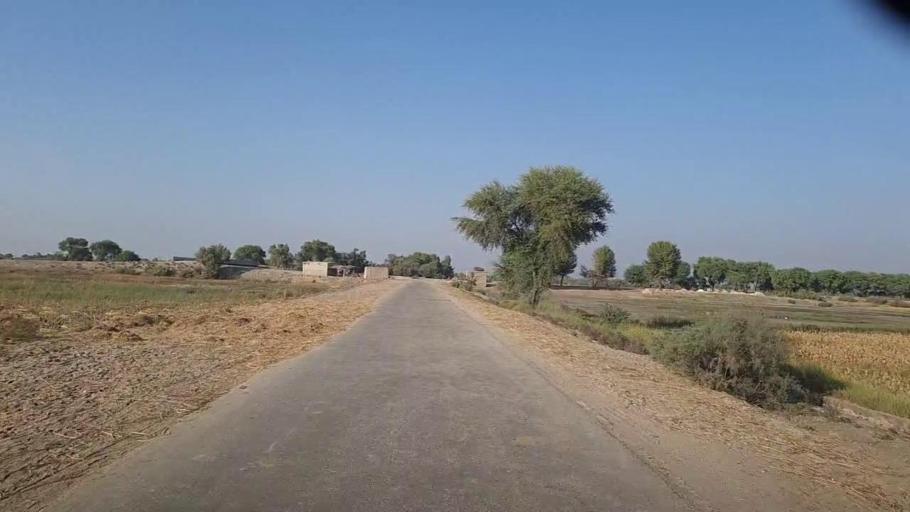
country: PK
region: Sindh
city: Tangwani
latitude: 28.2990
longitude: 68.9519
